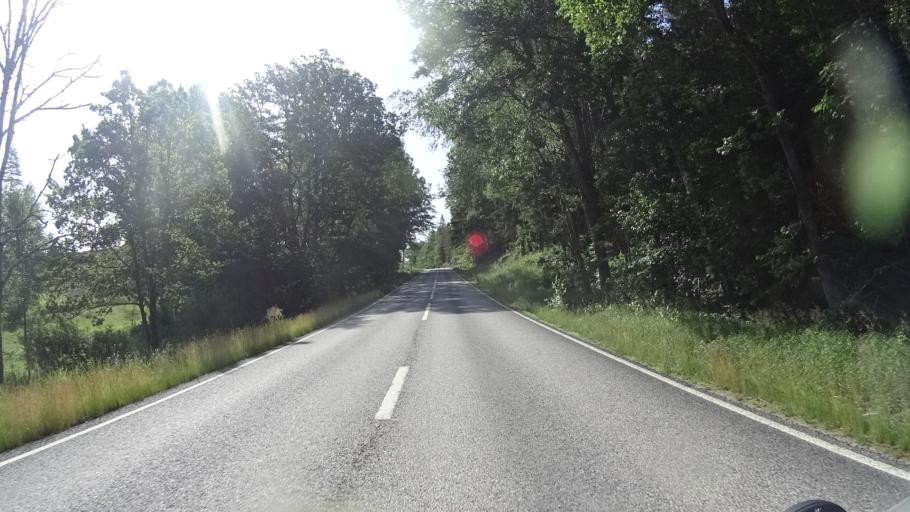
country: SE
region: Kalmar
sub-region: Vasterviks Kommun
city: Overum
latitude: 58.0764
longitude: 16.1876
